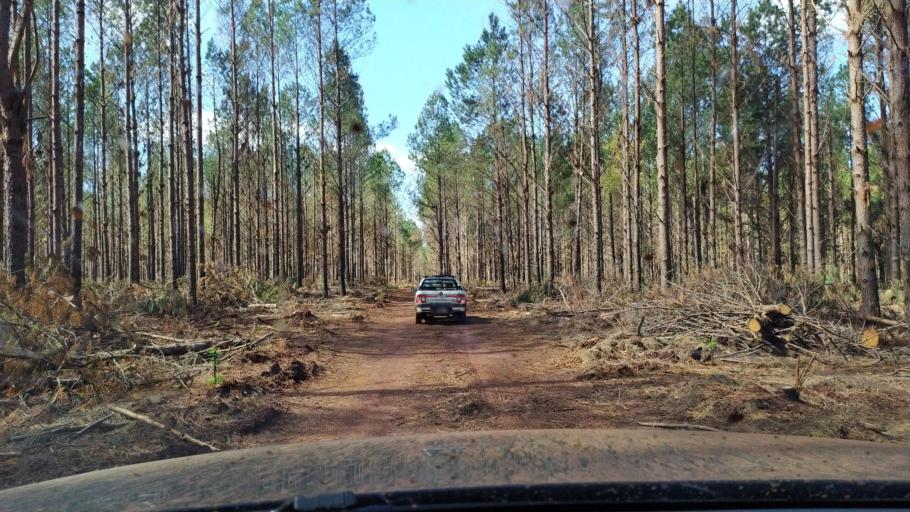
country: AR
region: Corrientes
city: Santo Tome
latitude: -28.4095
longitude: -56.0140
